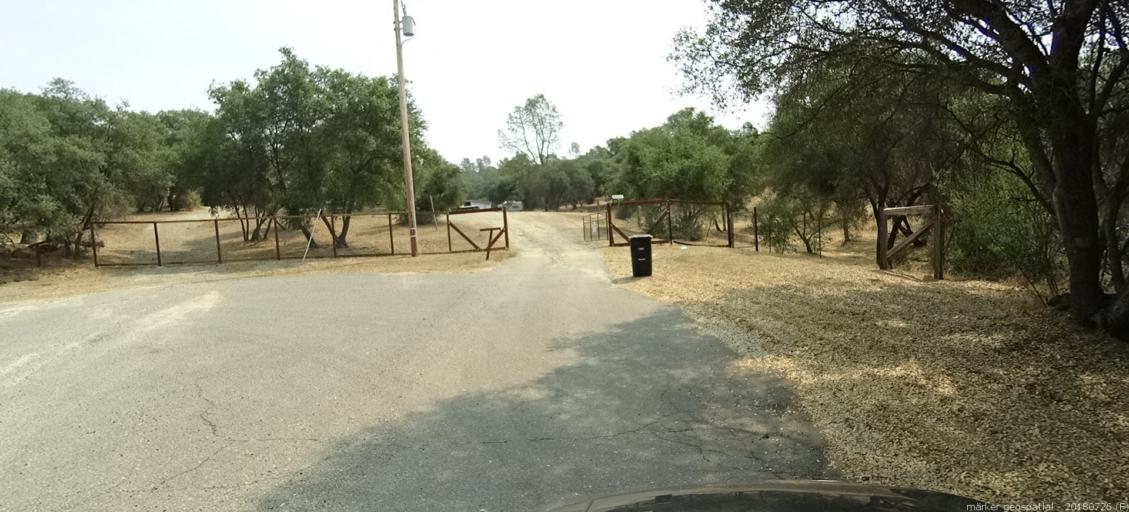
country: US
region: California
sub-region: Madera County
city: Coarsegold
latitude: 37.2421
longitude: -119.7018
